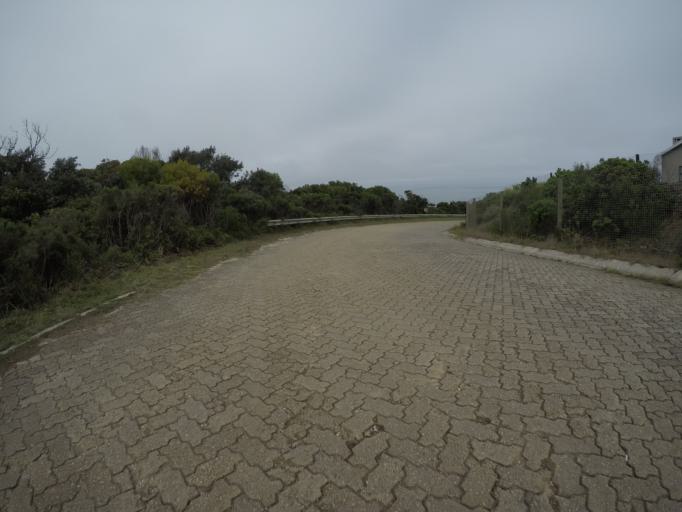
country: ZA
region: Eastern Cape
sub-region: Cacadu District Municipality
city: Kareedouw
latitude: -34.0739
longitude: 24.2330
